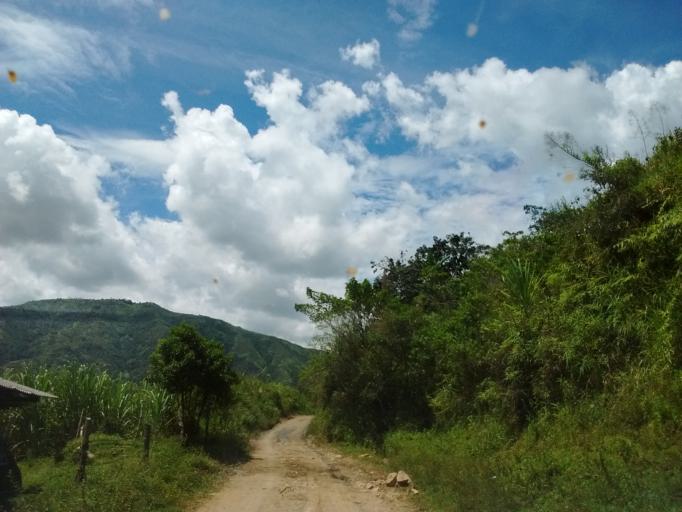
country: CO
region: Cauca
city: Villa Rica
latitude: 2.6524
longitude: -76.7706
